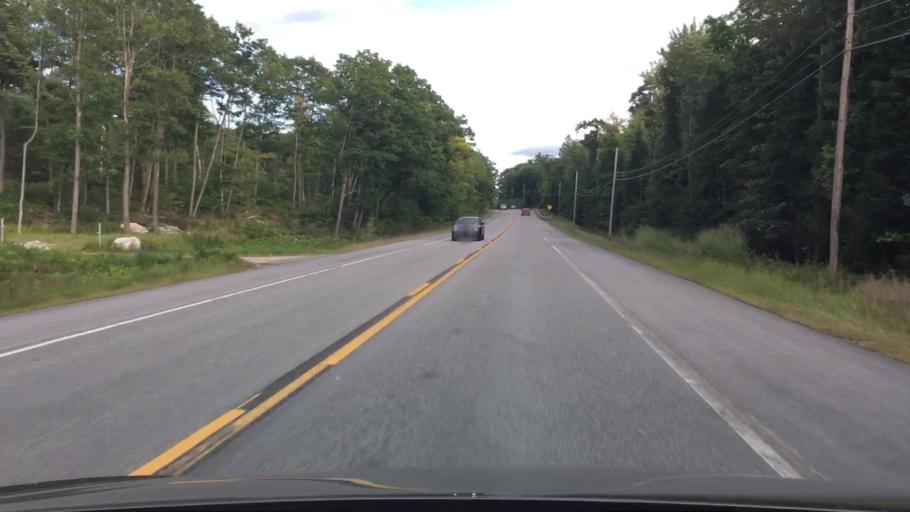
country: US
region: Maine
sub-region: Cumberland County
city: Bridgton
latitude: 44.0673
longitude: -70.7622
